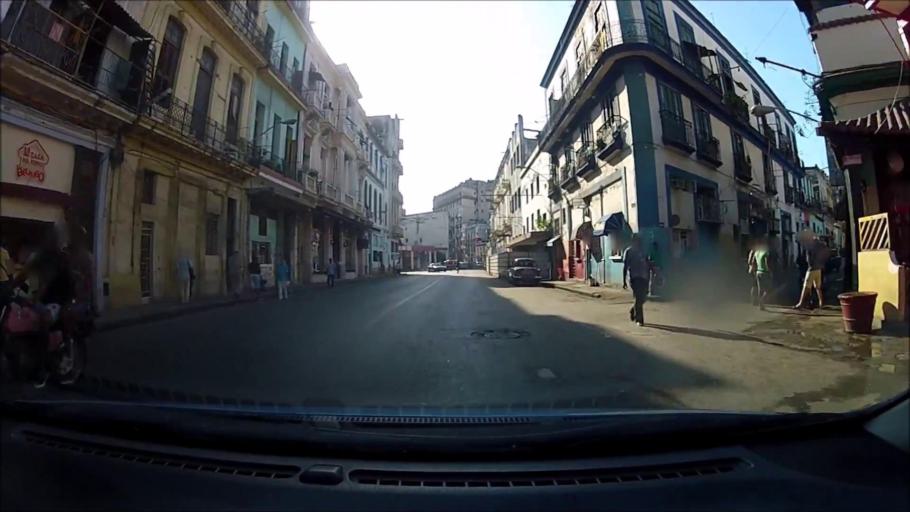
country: CU
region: La Habana
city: Centro Habana
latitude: 23.1348
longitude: -82.3638
